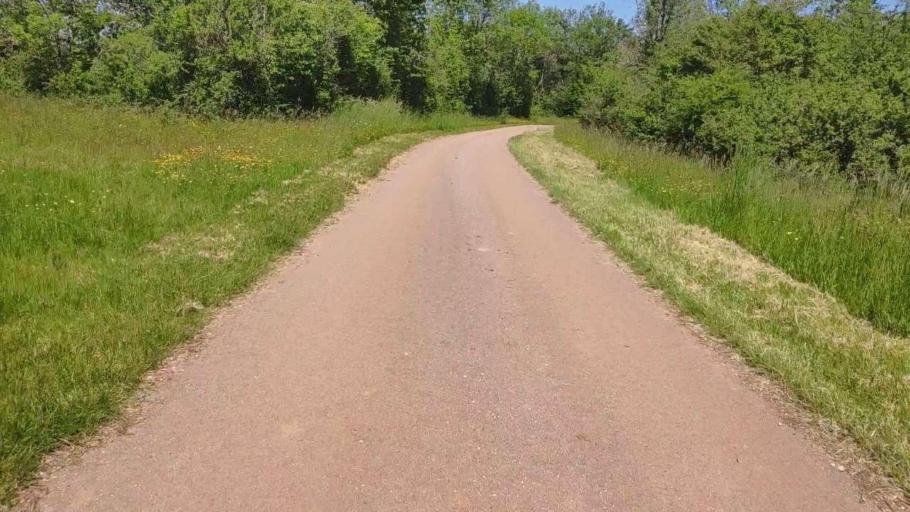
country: FR
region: Franche-Comte
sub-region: Departement du Jura
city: Perrigny
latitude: 46.7231
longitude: 5.6454
